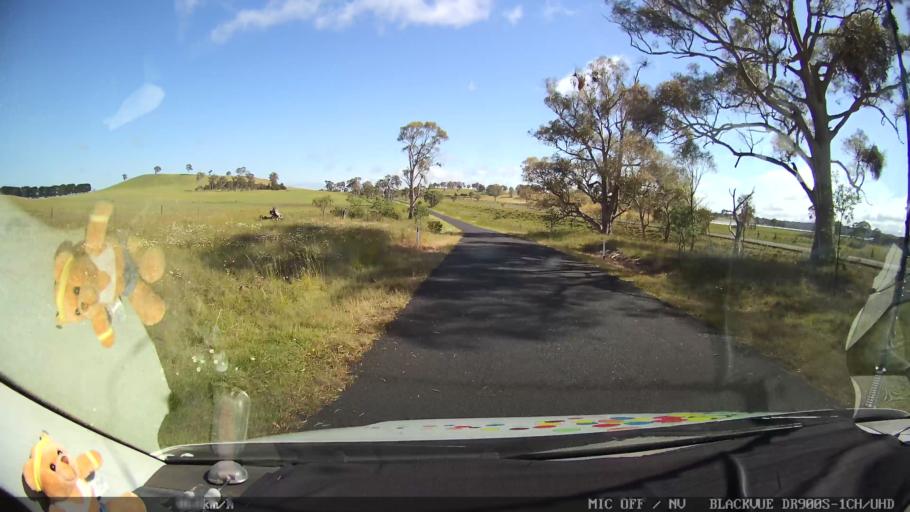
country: AU
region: New South Wales
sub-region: Guyra
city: Guyra
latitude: -30.1708
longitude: 151.6849
